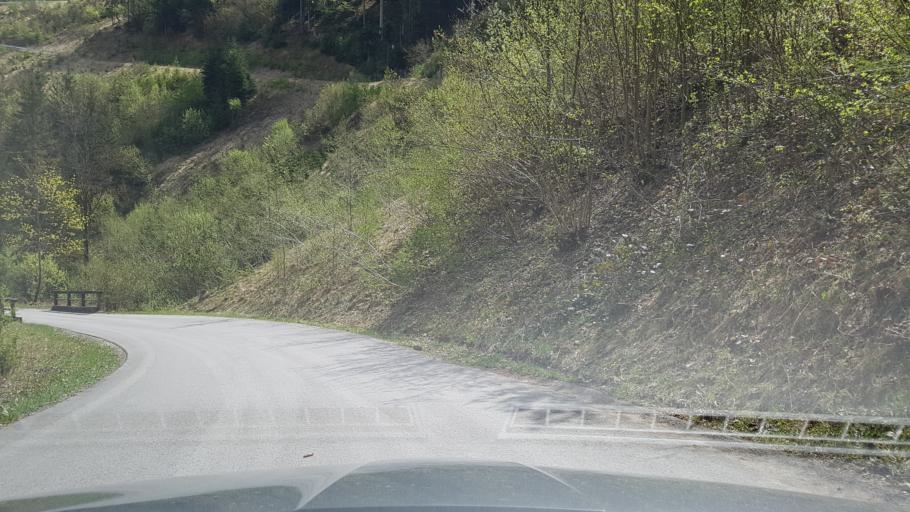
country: AT
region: Salzburg
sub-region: Politischer Bezirk Sankt Johann im Pongau
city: Werfen
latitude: 47.4588
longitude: 13.1854
